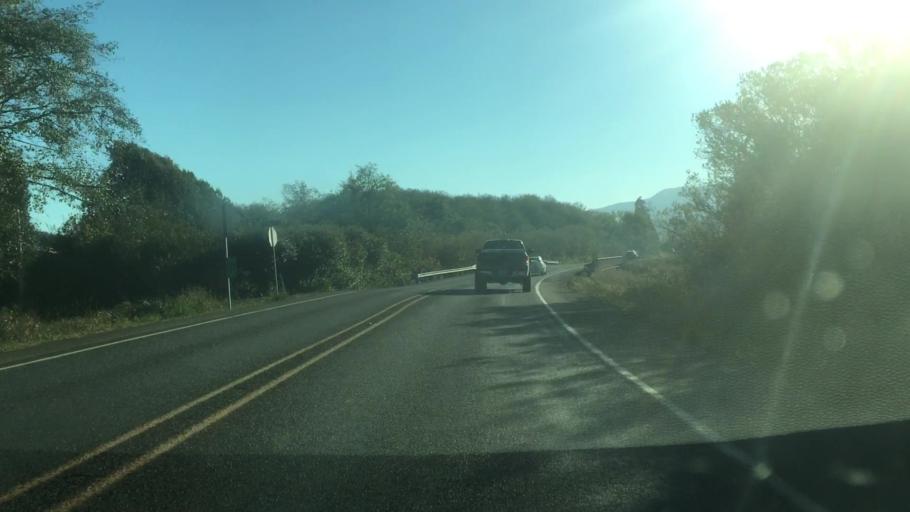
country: US
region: Oregon
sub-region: Clatsop County
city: Astoria
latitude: 46.3745
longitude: -123.8030
